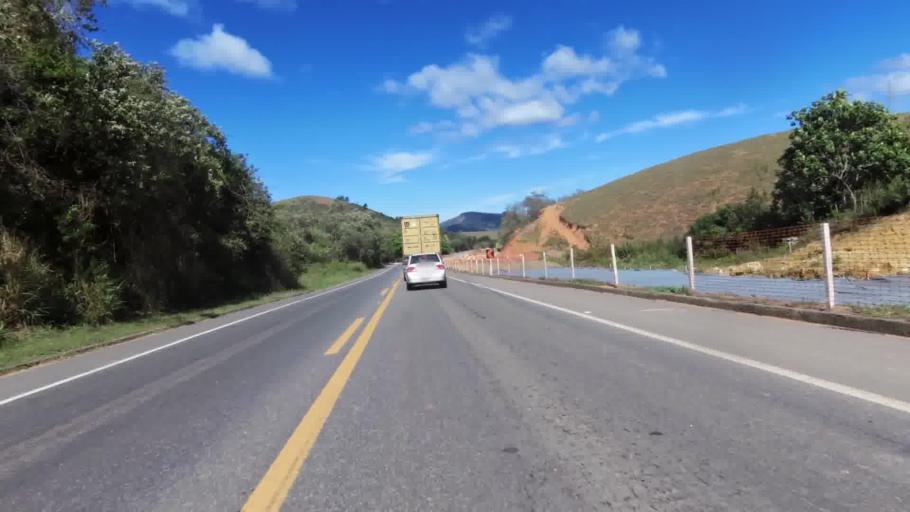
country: BR
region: Espirito Santo
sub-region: Iconha
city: Iconha
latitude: -20.7300
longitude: -40.7445
